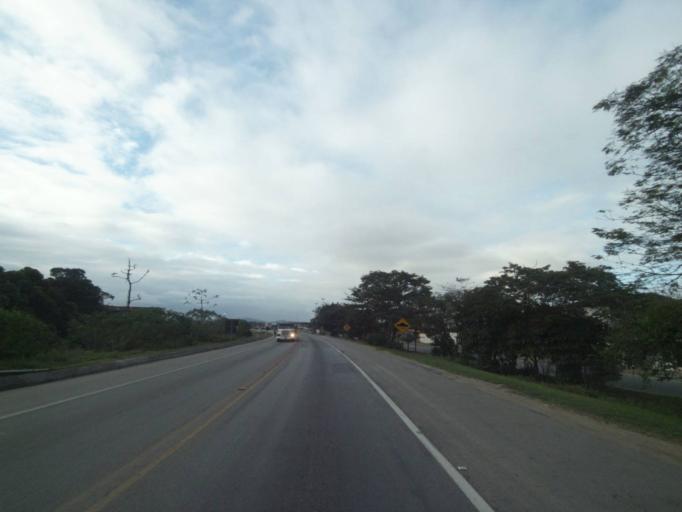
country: BR
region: Parana
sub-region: Paranagua
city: Paranagua
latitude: -25.5317
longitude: -48.5496
